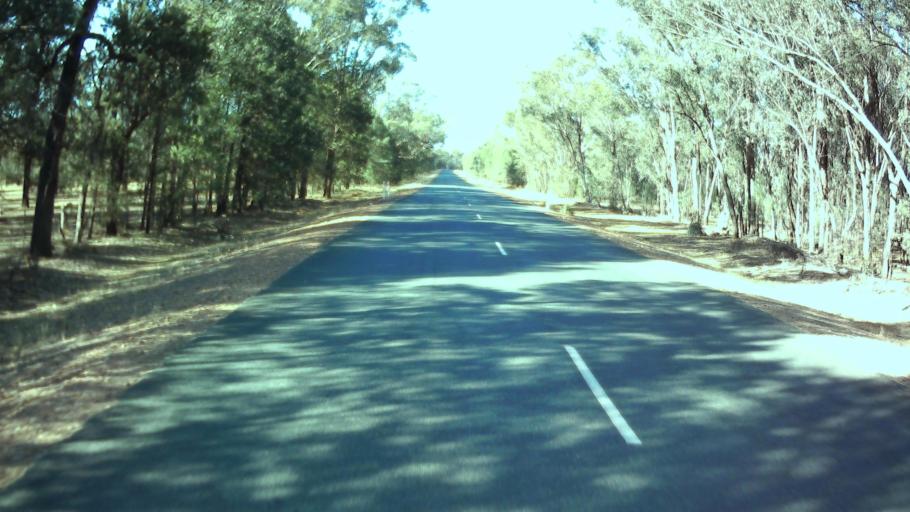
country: AU
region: New South Wales
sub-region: Weddin
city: Grenfell
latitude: -34.0254
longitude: 148.0975
